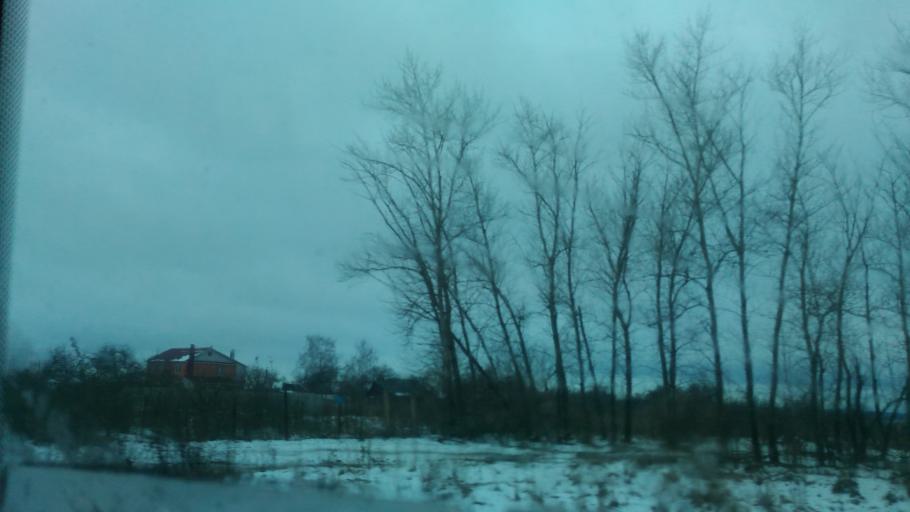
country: RU
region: Tula
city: Bolokhovo
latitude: 54.0698
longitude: 37.7953
